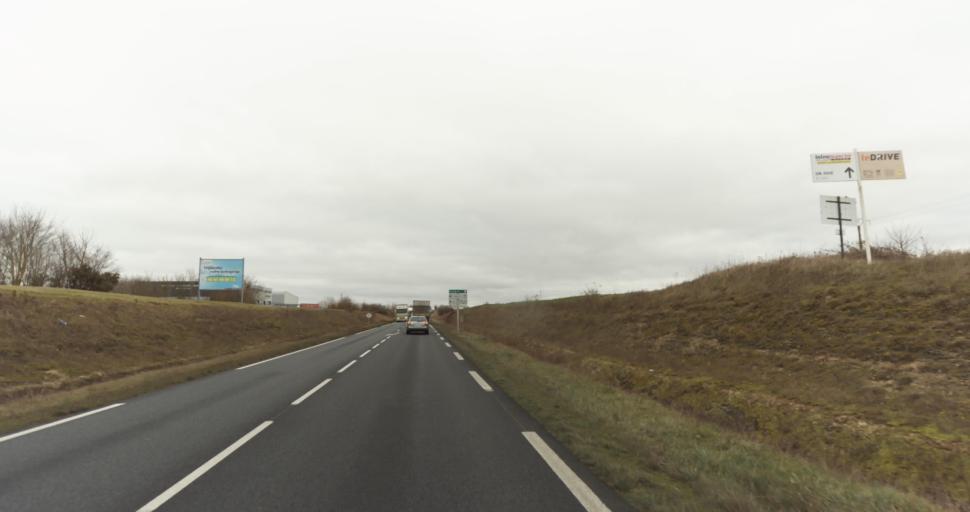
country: FR
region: Pays de la Loire
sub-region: Departement de Maine-et-Loire
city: Doue-la-Fontaine
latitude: 47.1917
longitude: -0.2437
